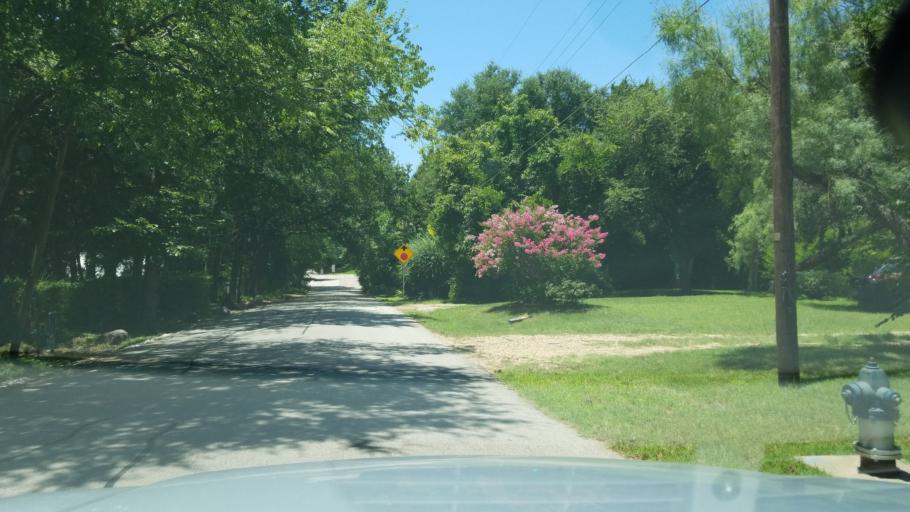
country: US
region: Texas
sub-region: Dallas County
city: Irving
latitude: 32.8121
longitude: -96.9241
